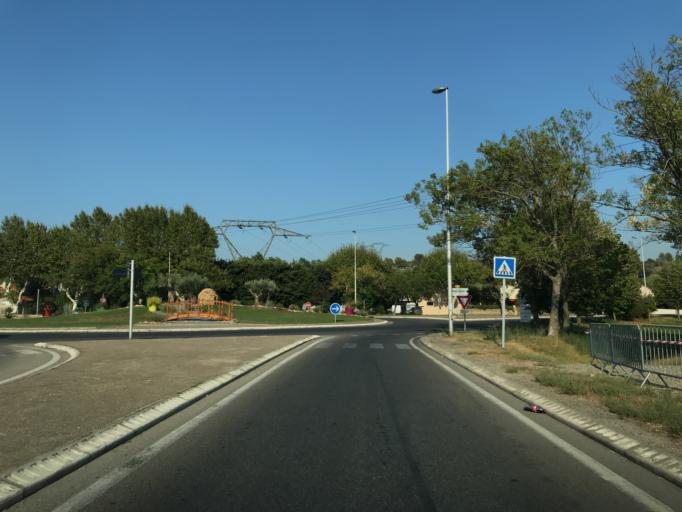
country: FR
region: Provence-Alpes-Cote d'Azur
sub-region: Departement des Bouches-du-Rhone
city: Miramas
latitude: 43.5712
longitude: 5.0181
